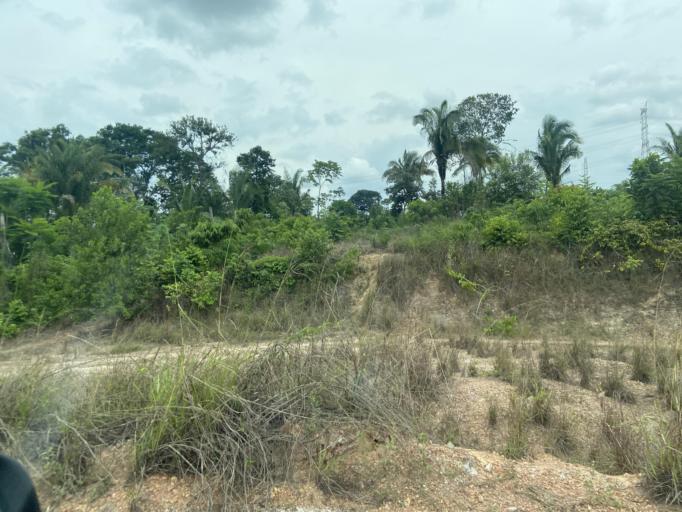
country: BR
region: Para
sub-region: Maraba
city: Maraba
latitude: -5.4256
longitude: -49.1158
